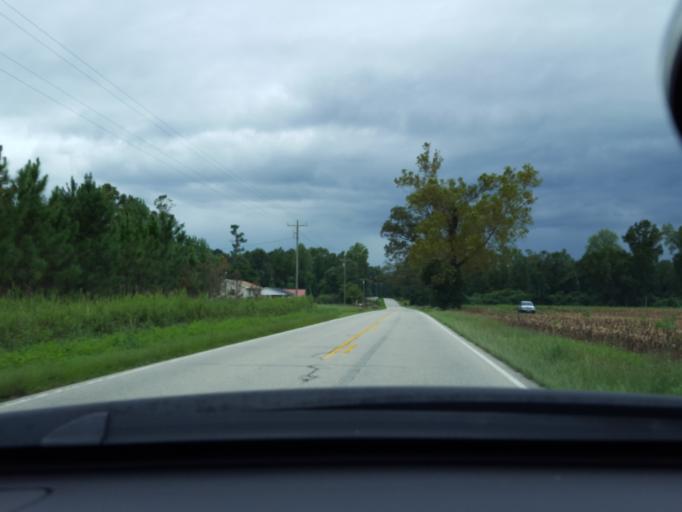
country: US
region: North Carolina
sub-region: Duplin County
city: Rose Hill
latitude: 34.8046
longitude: -78.2048
